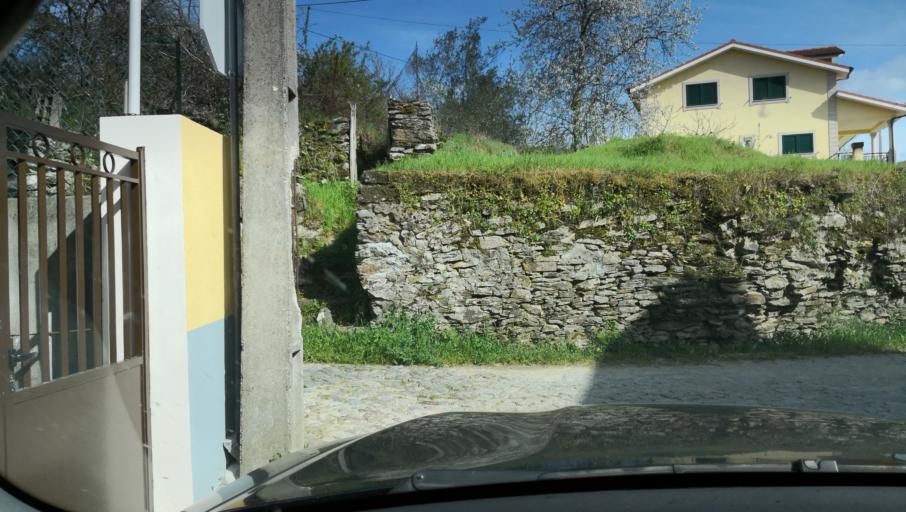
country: PT
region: Vila Real
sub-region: Sabrosa
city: Vilela
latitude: 41.2533
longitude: -7.6638
